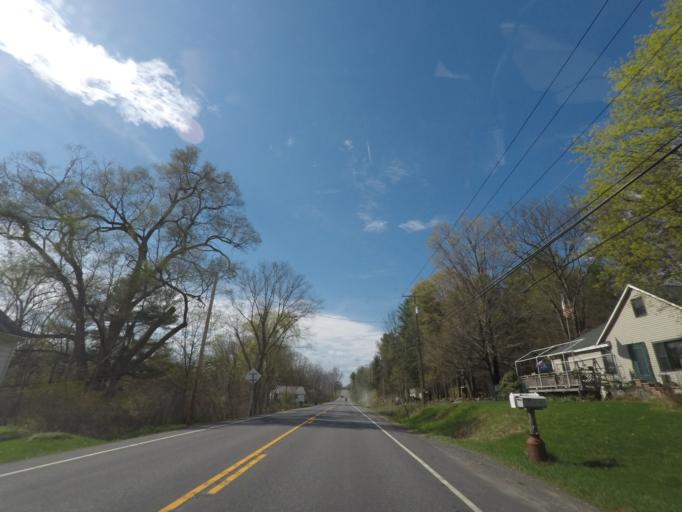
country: US
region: New York
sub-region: Greene County
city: Cairo
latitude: 42.3372
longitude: -74.0236
